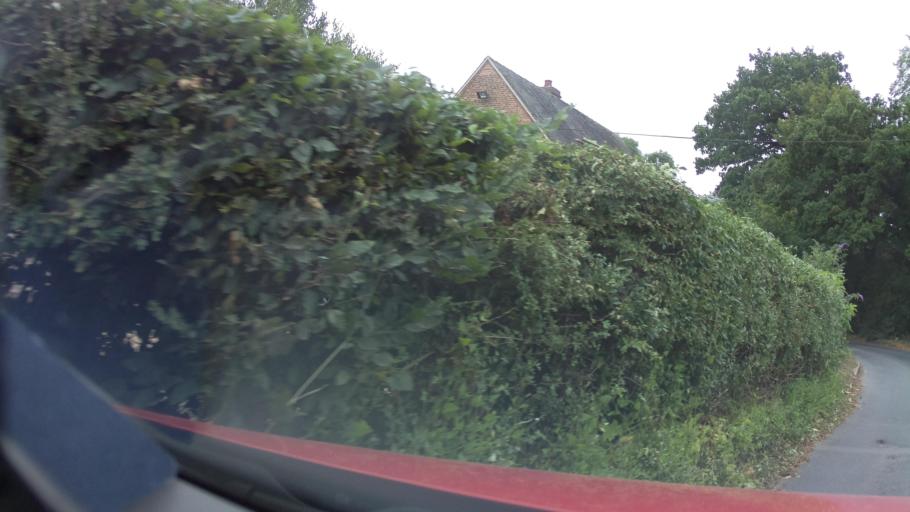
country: GB
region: England
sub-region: Derbyshire
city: Swadlincote
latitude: 52.7935
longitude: -1.5372
